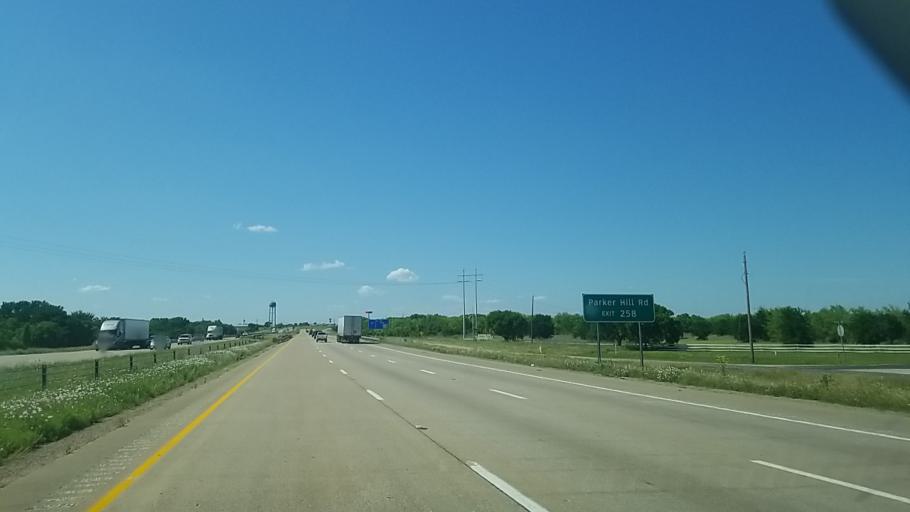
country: US
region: Texas
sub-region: Ellis County
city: Palmer
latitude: 32.4035
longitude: -96.6563
